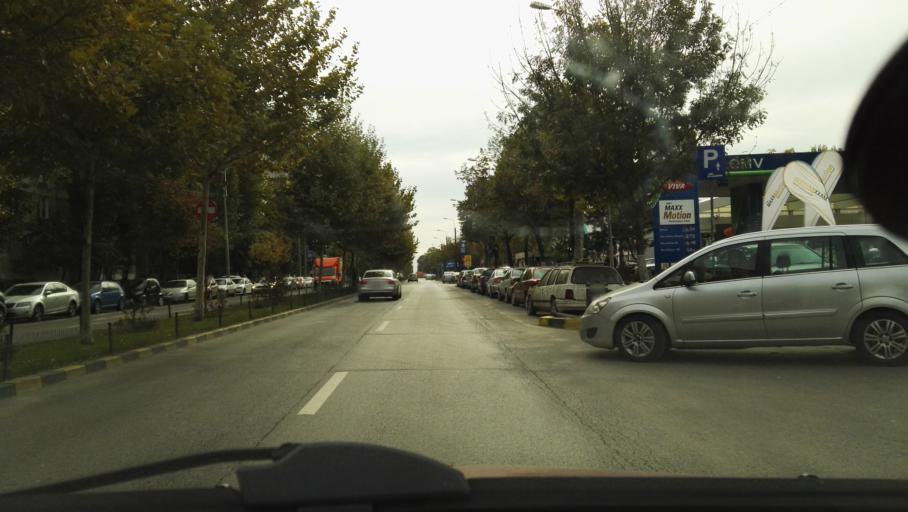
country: RO
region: Ilfov
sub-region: Comuna Popesti-Leordeni
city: Popesti-Leordeni
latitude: 44.3903
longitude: 26.1246
